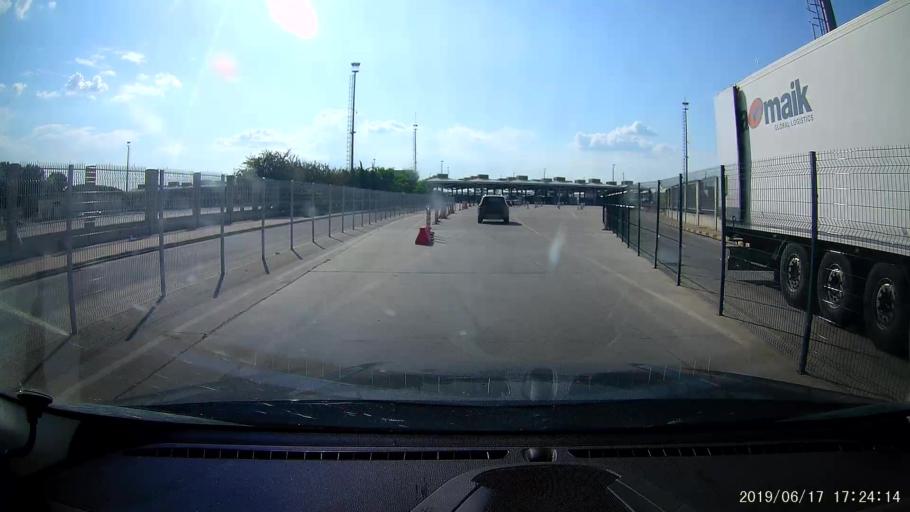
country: GR
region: East Macedonia and Thrace
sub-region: Nomos Evrou
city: Rizia
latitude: 41.7150
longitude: 26.3617
